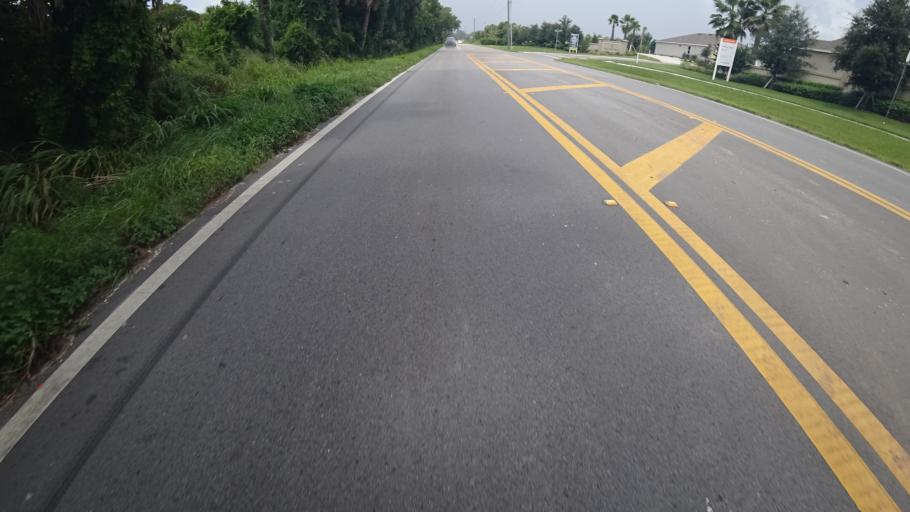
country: US
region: Florida
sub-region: Manatee County
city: Ellenton
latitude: 27.5469
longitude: -82.5175
